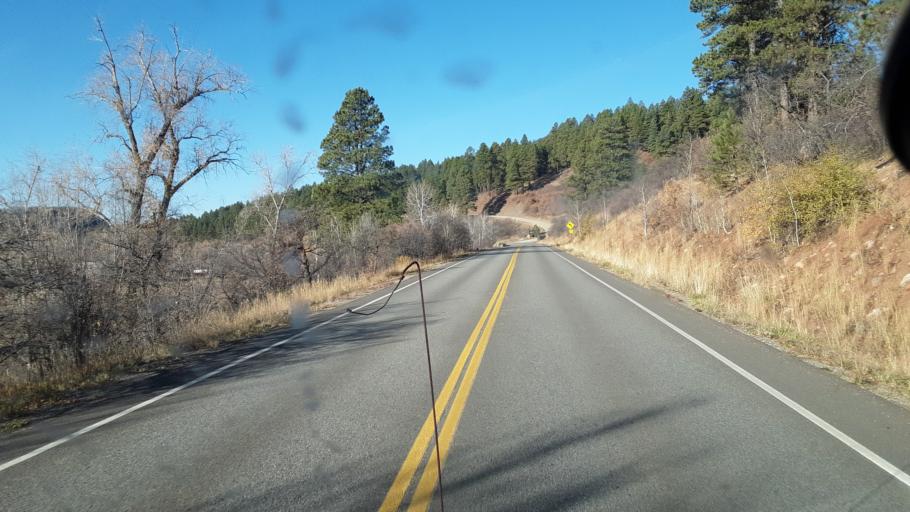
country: US
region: Colorado
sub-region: La Plata County
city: Bayfield
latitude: 37.3538
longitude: -107.6854
